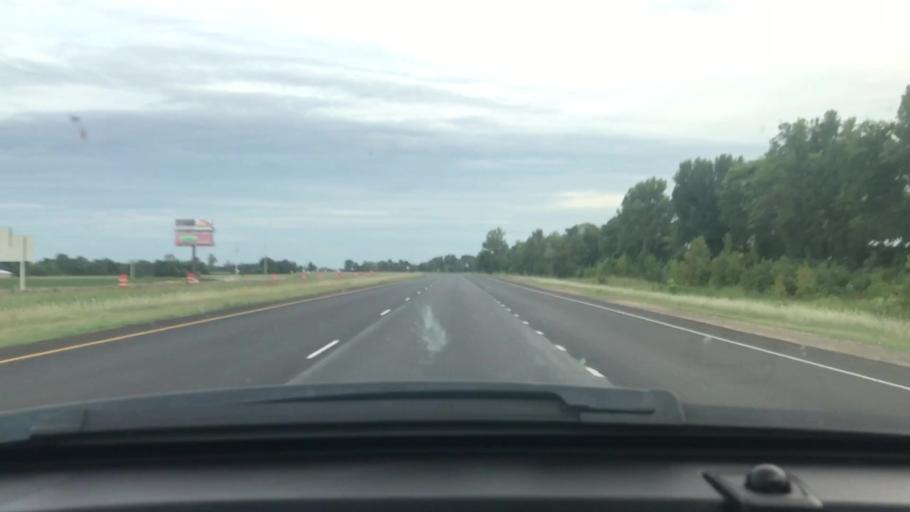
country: US
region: Arkansas
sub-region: Poinsett County
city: Trumann
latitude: 35.6742
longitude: -90.5530
